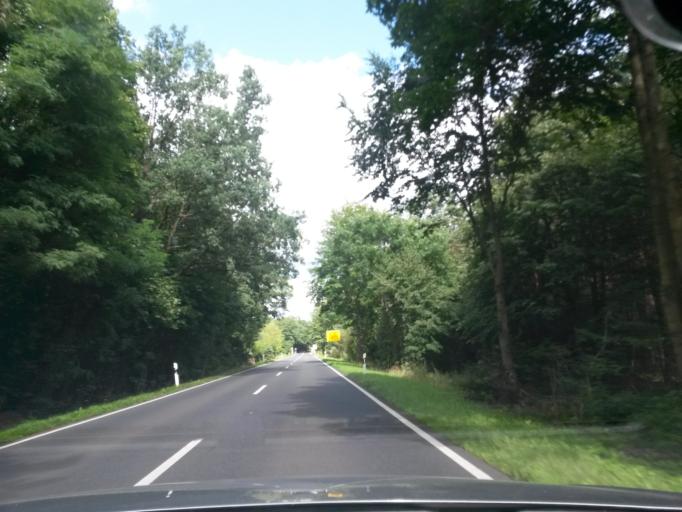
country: DE
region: Brandenburg
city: Chorin
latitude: 52.9162
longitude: 13.9011
